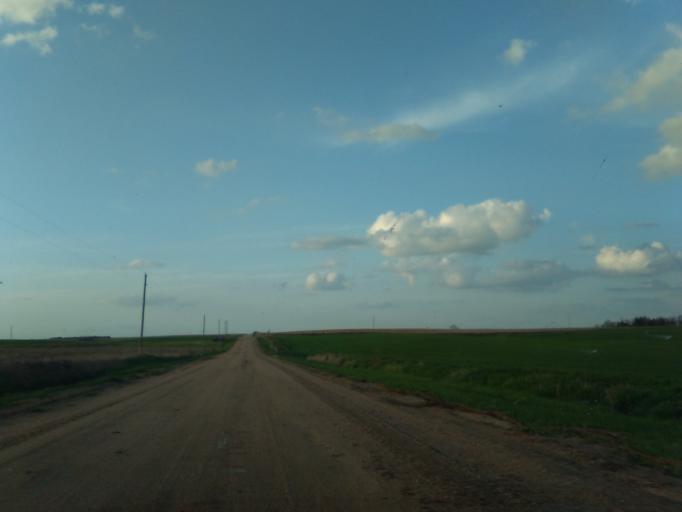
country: US
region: Nebraska
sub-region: Webster County
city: Red Cloud
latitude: 40.2169
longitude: -98.3680
